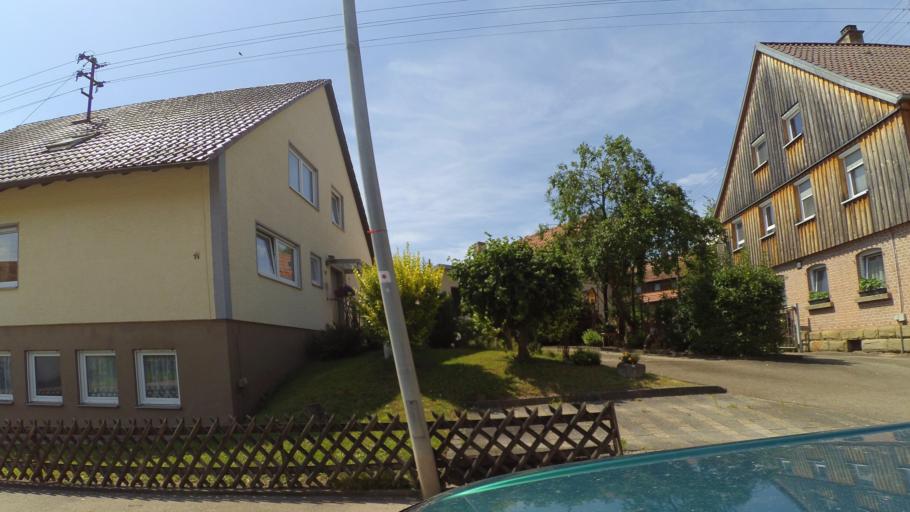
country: DE
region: Baden-Wuerttemberg
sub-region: Regierungsbezirk Stuttgart
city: Eschach
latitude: 48.9448
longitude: 9.8569
